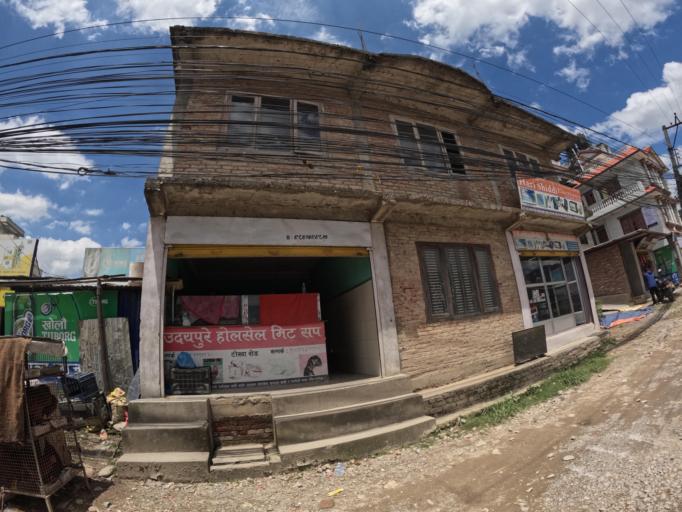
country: NP
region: Central Region
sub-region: Bagmati Zone
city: Kathmandu
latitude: 27.7588
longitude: 85.3278
